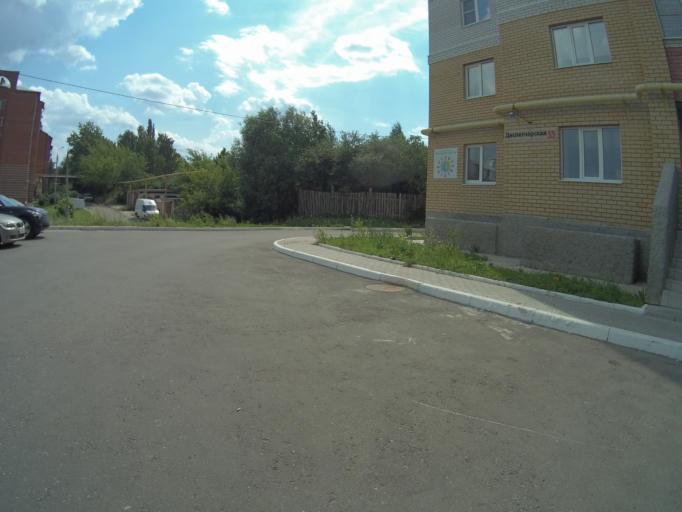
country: RU
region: Vladimir
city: Vladimir
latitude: 56.1329
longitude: 40.3813
